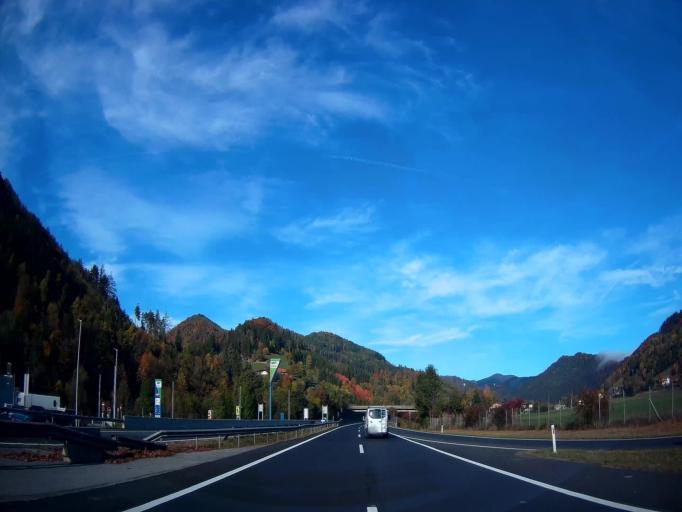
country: AT
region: Styria
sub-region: Politischer Bezirk Graz-Umgebung
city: Deutschfeistritz
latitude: 47.2059
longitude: 15.3169
